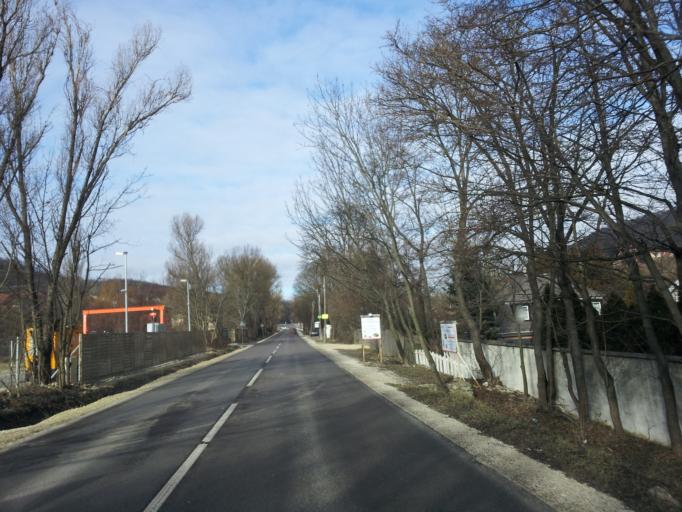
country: HU
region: Pest
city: Solymar
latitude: 47.5568
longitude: 18.9252
